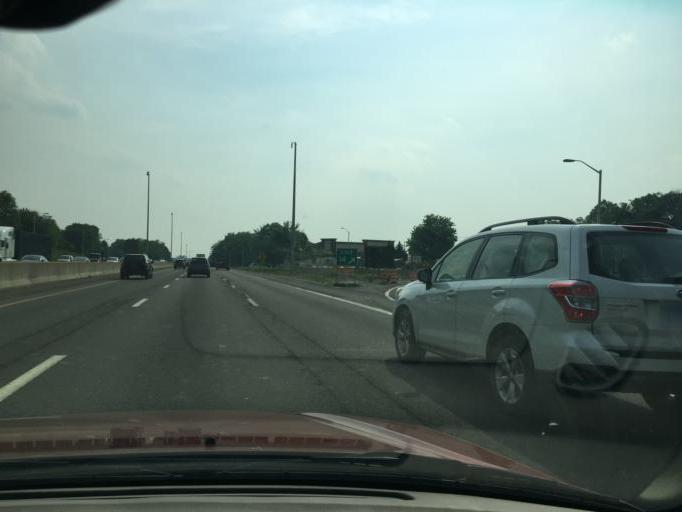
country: US
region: Connecticut
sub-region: Fairfield County
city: Norwalk
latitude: 41.1034
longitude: -73.4319
